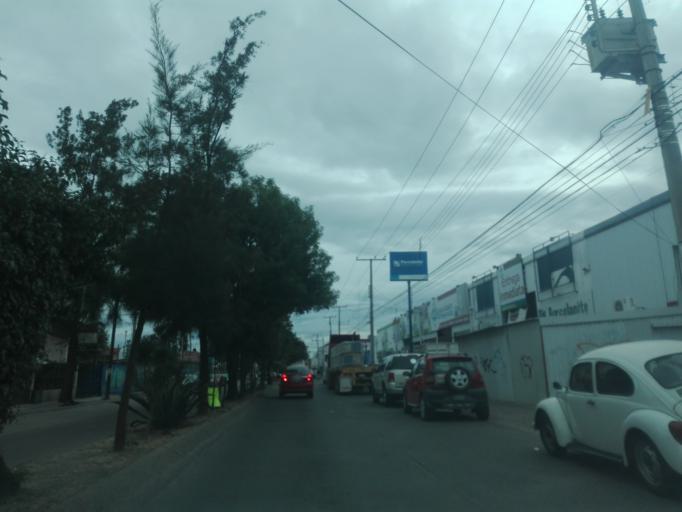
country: MX
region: Guanajuato
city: Leon
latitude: 21.1047
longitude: -101.6725
